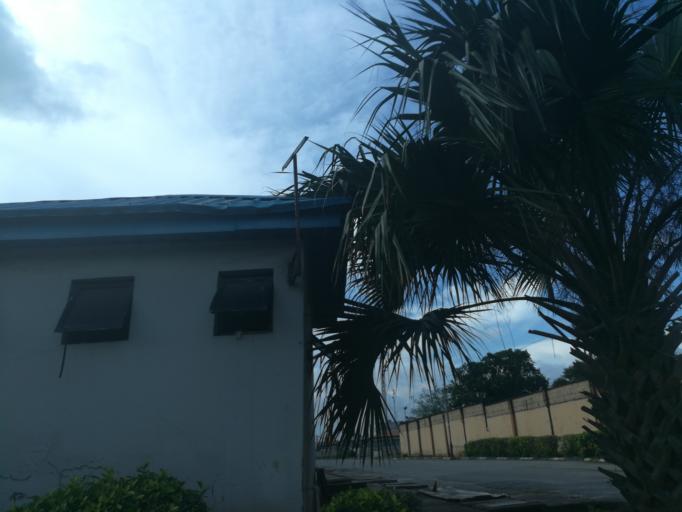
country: NG
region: Lagos
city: Ikeja
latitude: 6.6151
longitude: 3.3555
